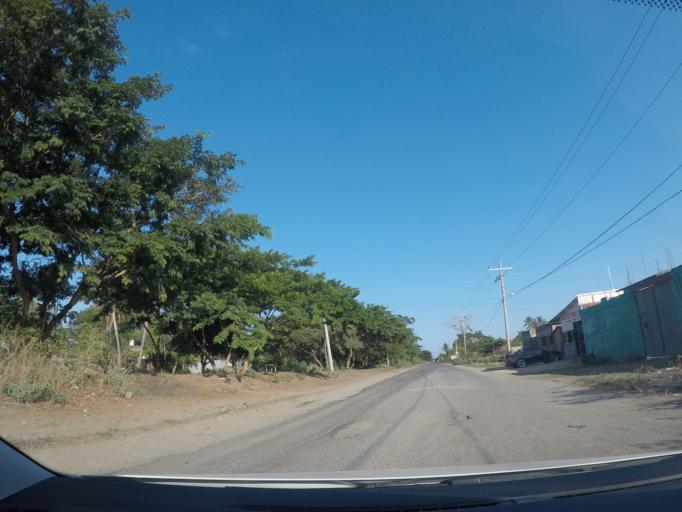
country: MX
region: Oaxaca
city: Juchitan de Zaragoza
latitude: 16.4260
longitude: -95.0312
